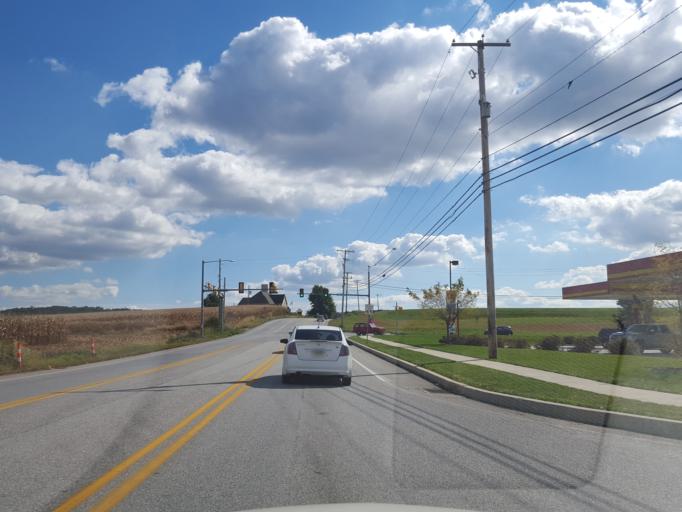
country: US
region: Pennsylvania
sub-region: York County
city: Yoe
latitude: 39.9461
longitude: -76.6472
